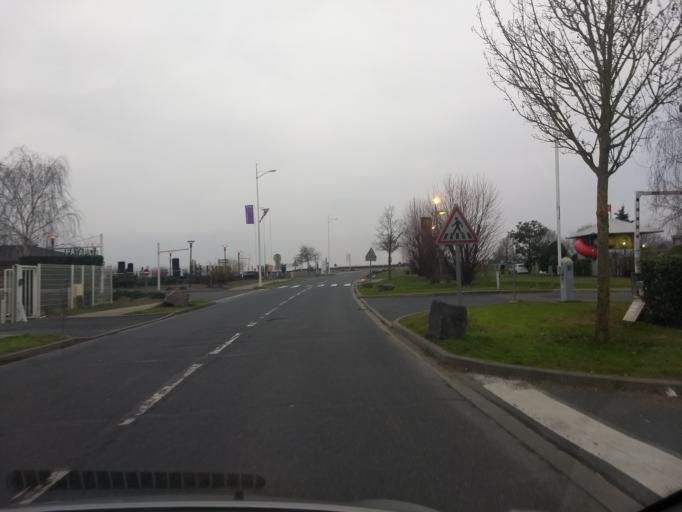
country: FR
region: Centre
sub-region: Departement de l'Indre
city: Deols
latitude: 46.8516
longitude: 1.7038
